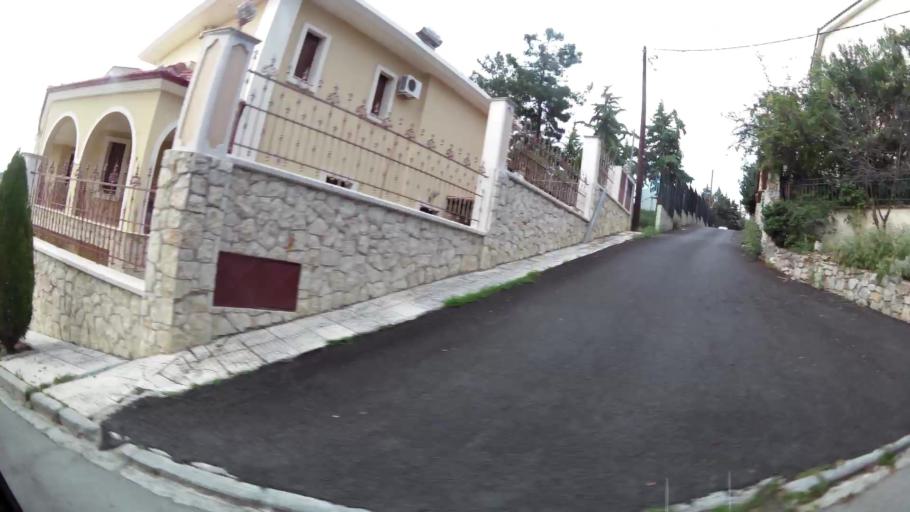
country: GR
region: Central Macedonia
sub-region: Nomos Thessalonikis
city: Pefka
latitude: 40.6629
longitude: 22.9852
